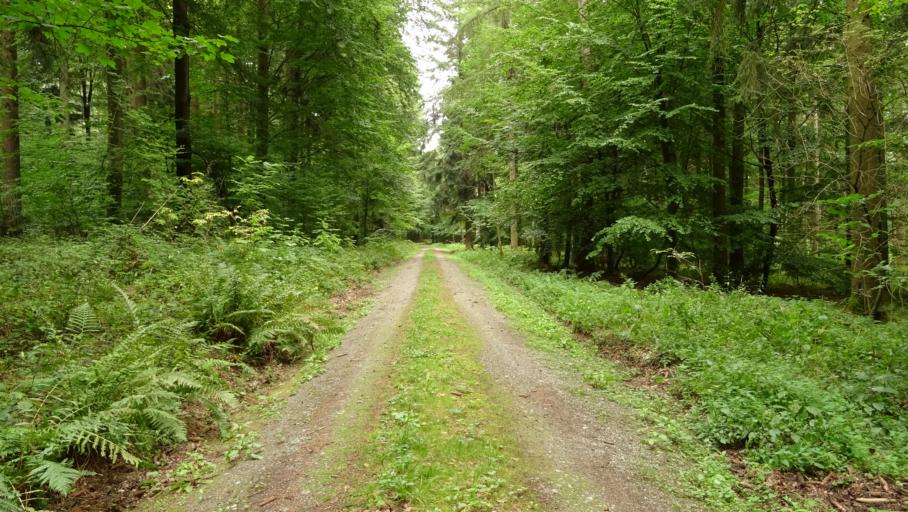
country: DE
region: Baden-Wuerttemberg
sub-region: Karlsruhe Region
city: Fahrenbach
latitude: 49.4094
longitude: 9.1163
